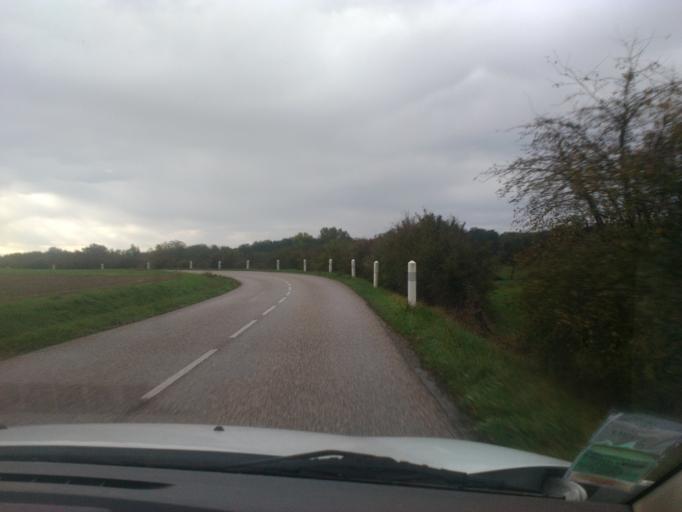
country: FR
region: Lorraine
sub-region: Departement des Vosges
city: Dogneville
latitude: 48.2646
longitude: 6.5018
